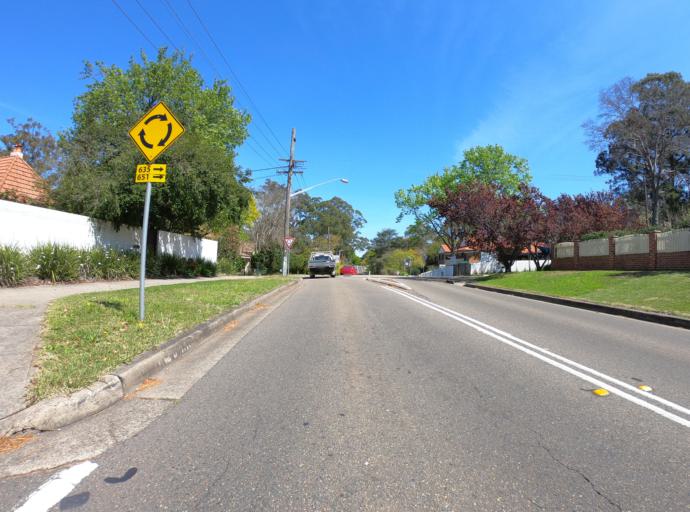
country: AU
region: New South Wales
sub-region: Hornsby Shire
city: Beecroft
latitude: -33.7516
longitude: 151.0621
